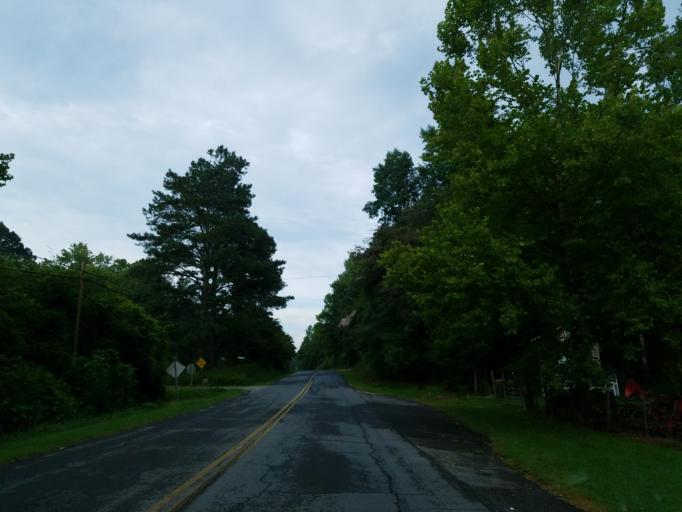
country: US
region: Georgia
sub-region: Fannin County
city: Blue Ridge
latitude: 34.7802
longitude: -84.3915
